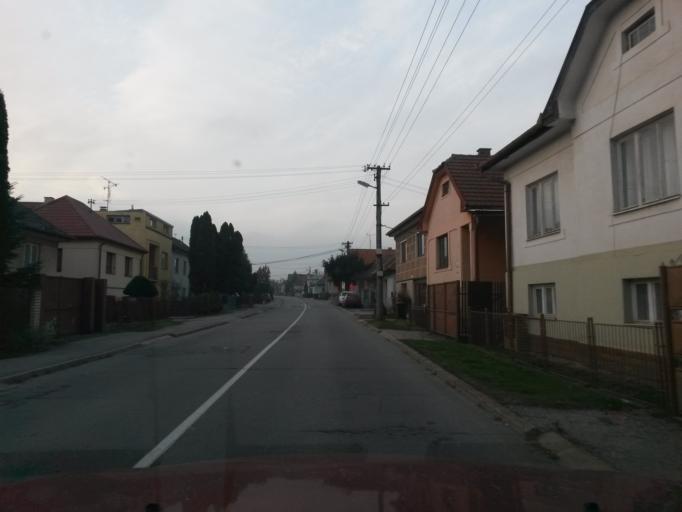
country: SK
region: Kosicky
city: Kosice
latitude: 48.7034
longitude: 21.2162
